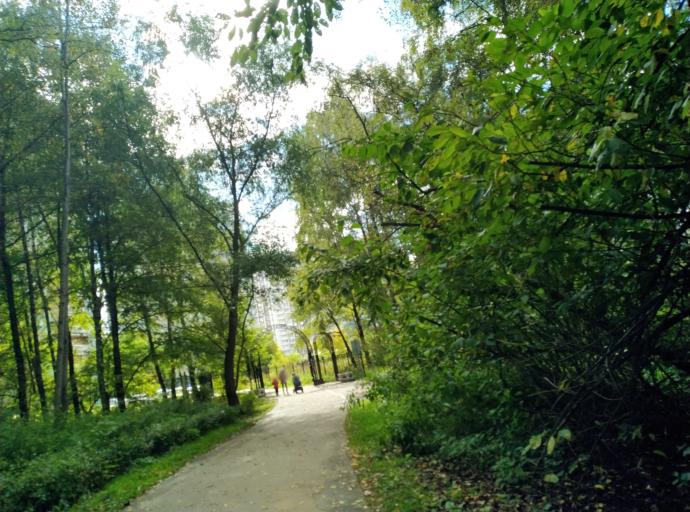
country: RU
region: Moscow
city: Khimki
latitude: 55.8644
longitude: 37.4185
